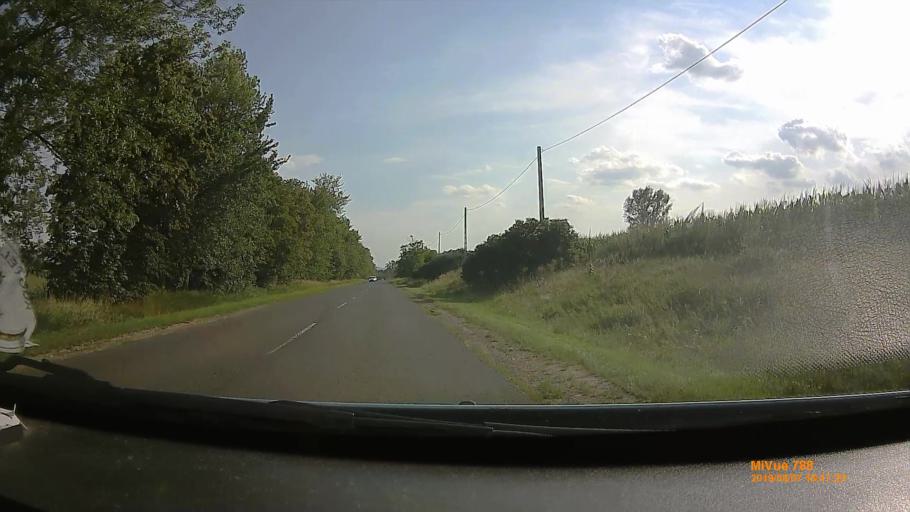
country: HU
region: Borsod-Abauj-Zemplen
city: Abaujszanto
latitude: 48.3421
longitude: 21.2080
